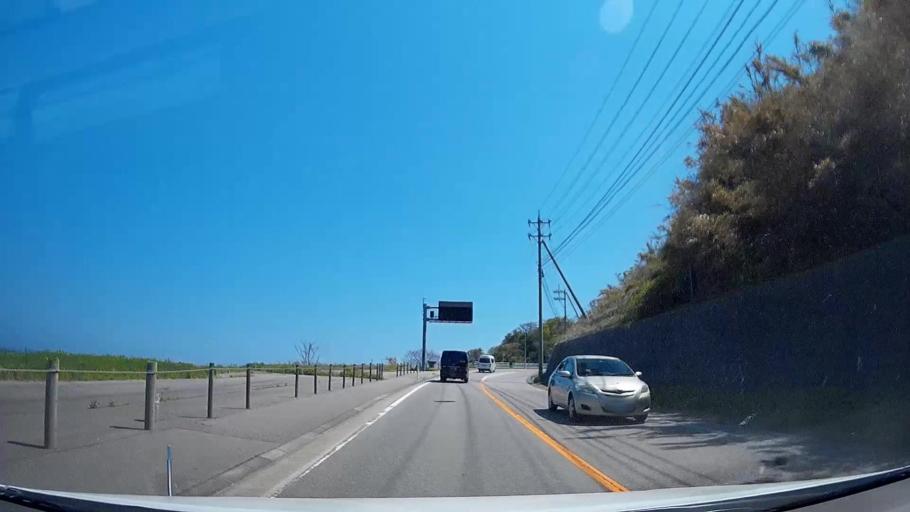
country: JP
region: Ishikawa
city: Nanao
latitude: 37.3968
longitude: 136.9301
